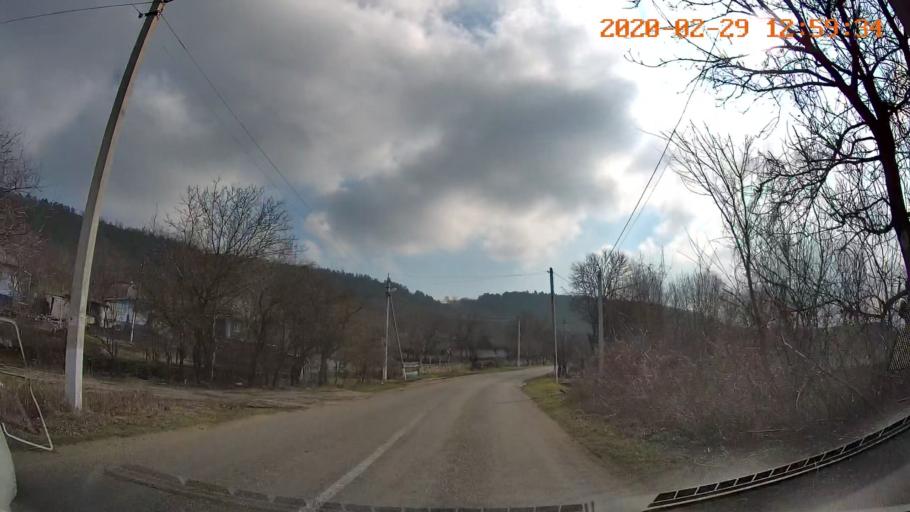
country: MD
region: Telenesti
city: Camenca
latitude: 48.0609
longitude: 28.7248
